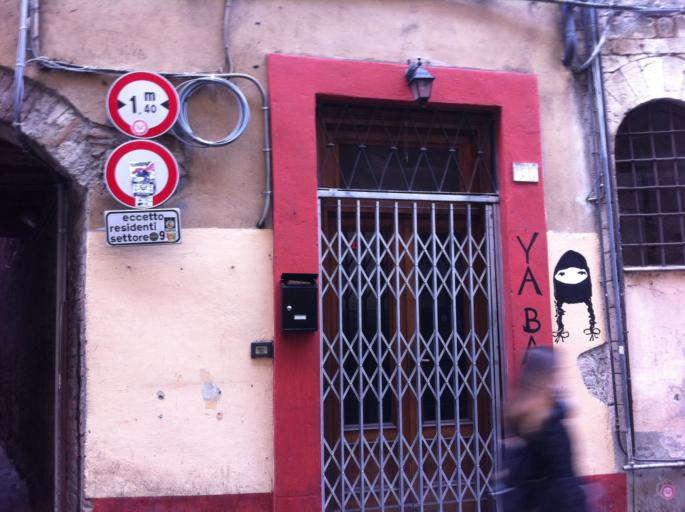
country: IT
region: Umbria
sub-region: Provincia di Perugia
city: Perugia
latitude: 43.1156
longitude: 12.3896
